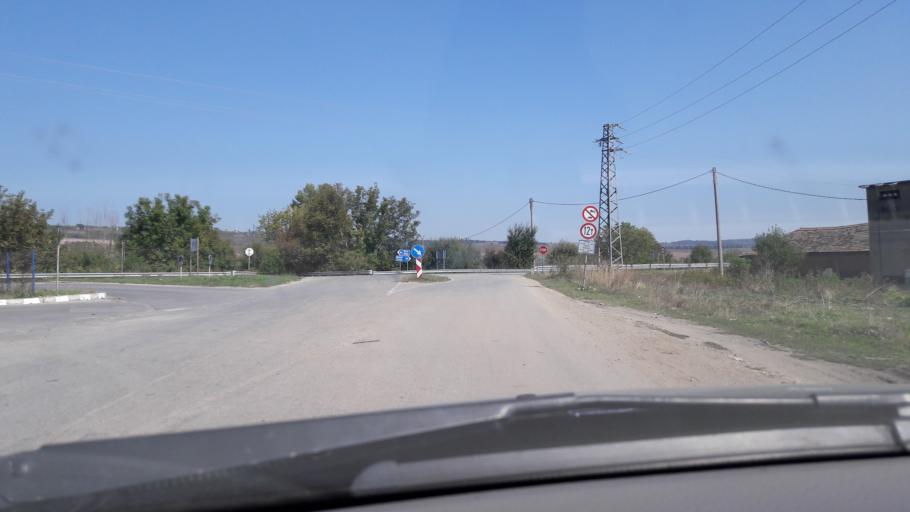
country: BG
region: Razgrad
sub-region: Obshtina Razgrad
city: Razgrad
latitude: 43.5480
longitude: 26.4781
